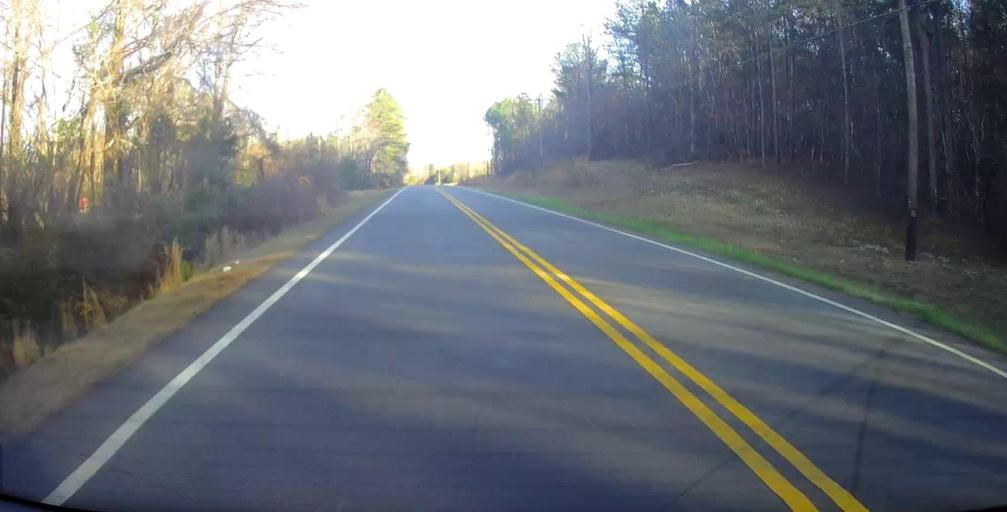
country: US
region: Georgia
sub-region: Meriwether County
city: Manchester
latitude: 32.8799
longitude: -84.6650
